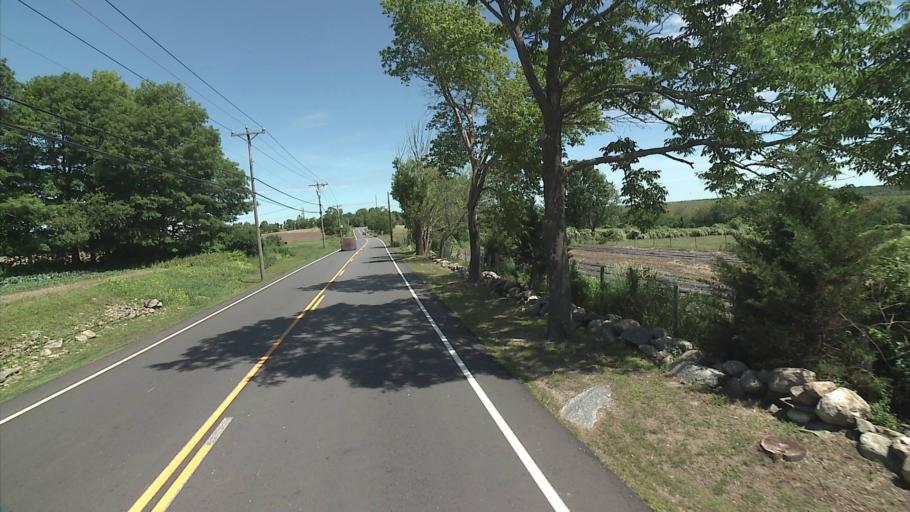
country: US
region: Connecticut
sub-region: Windham County
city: Moosup
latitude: 41.6538
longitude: -71.8479
